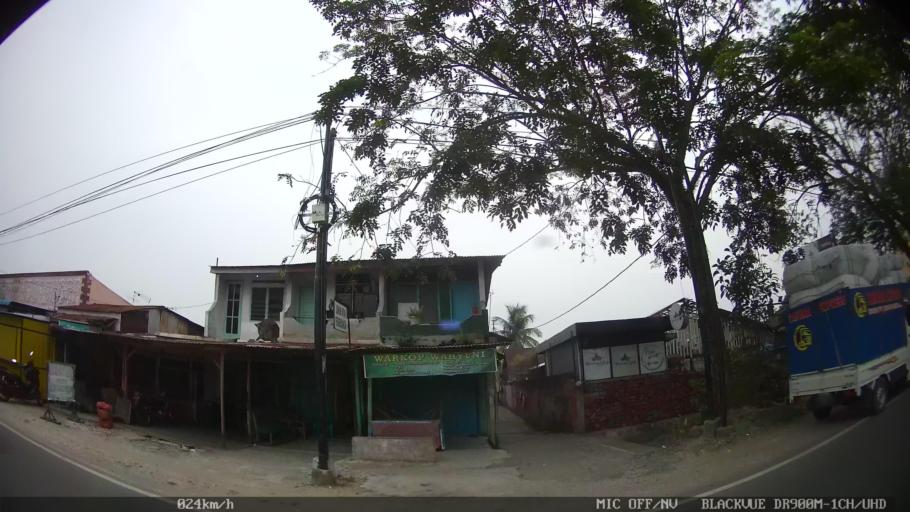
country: ID
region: North Sumatra
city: Medan
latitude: 3.5684
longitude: 98.7065
